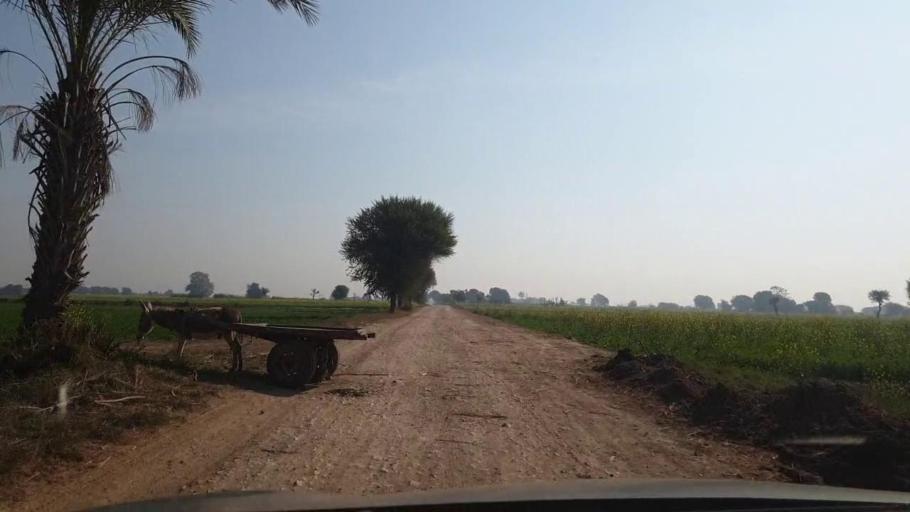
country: PK
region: Sindh
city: Tando Allahyar
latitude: 25.5935
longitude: 68.7331
